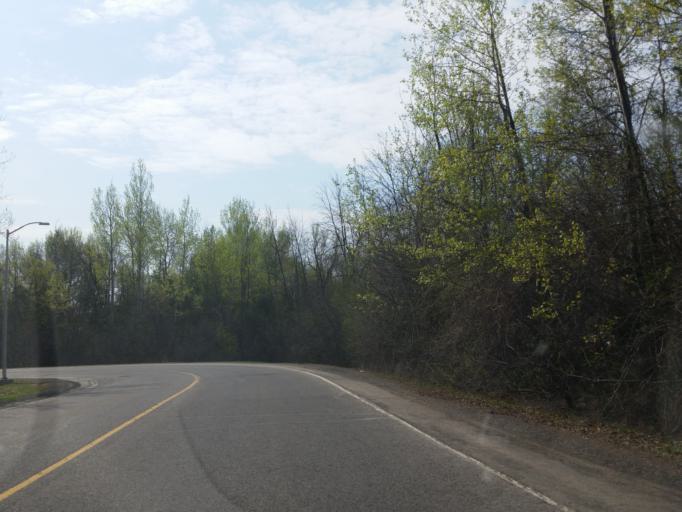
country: CA
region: Ontario
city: Ottawa
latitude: 45.4416
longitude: -75.6224
